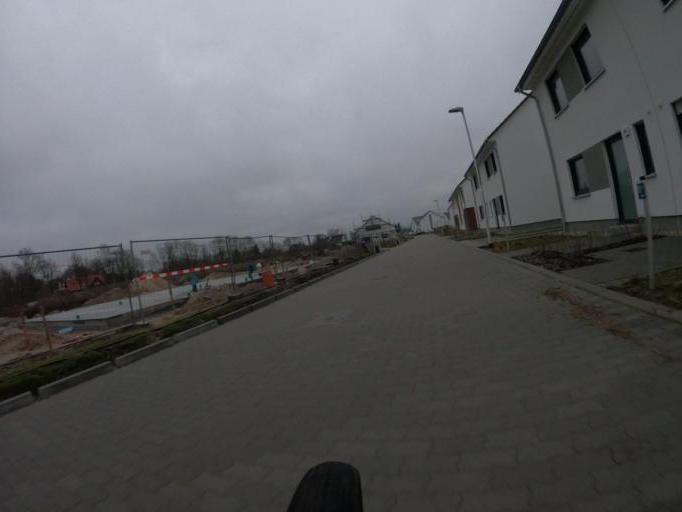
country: DE
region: Brandenburg
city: Schulzendorf
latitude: 52.3570
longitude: 13.5783
